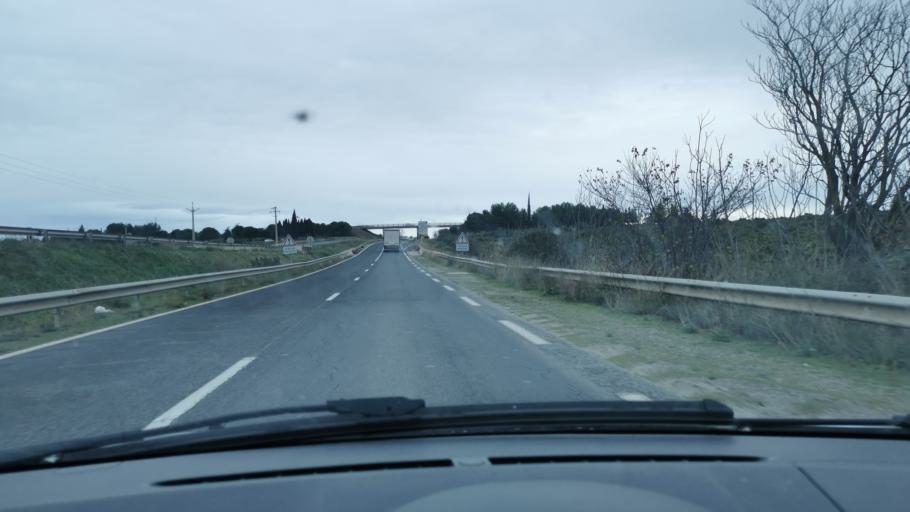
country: FR
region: Languedoc-Roussillon
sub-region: Departement de l'Herault
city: Saint-Jean-de-Vedas
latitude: 43.5421
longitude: 3.8231
